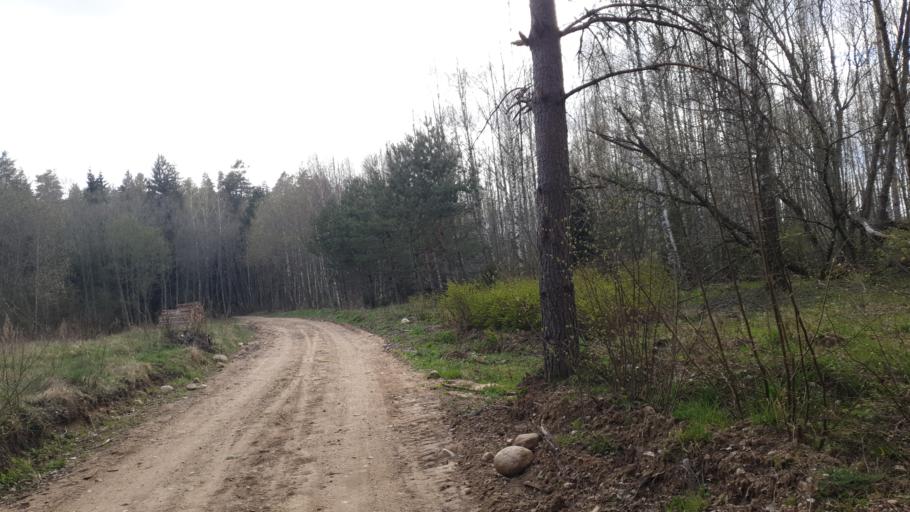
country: LT
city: Aukstadvaris
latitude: 54.5112
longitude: 24.6389
